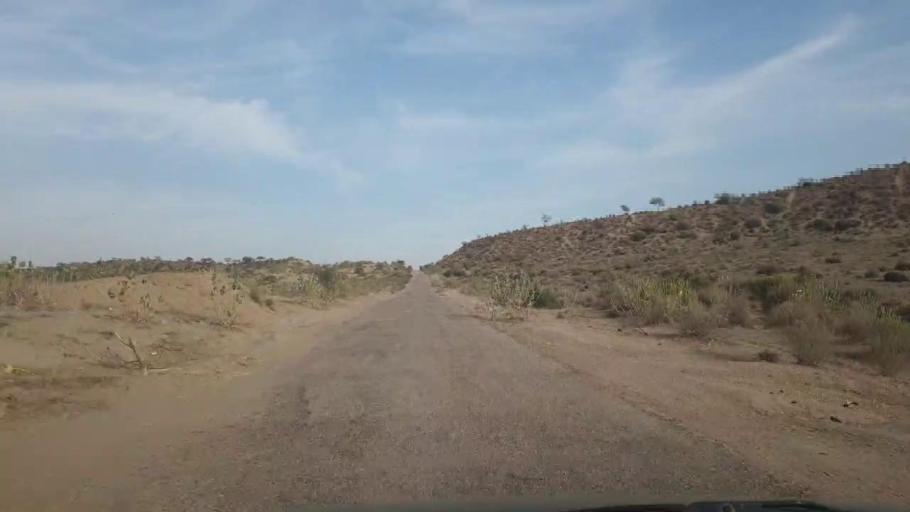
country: PK
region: Sindh
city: Nabisar
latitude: 25.0544
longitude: 69.6819
